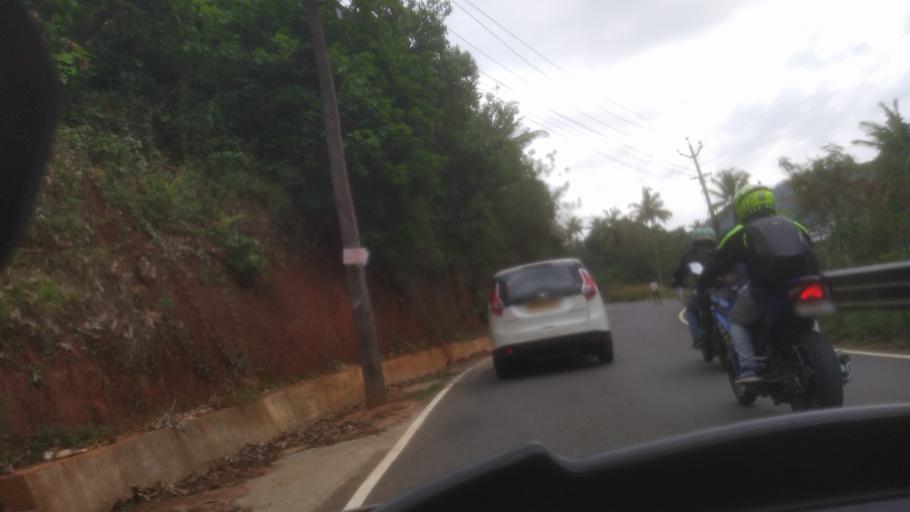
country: IN
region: Kerala
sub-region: Idukki
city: Idukki
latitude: 9.9595
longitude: 77.0090
